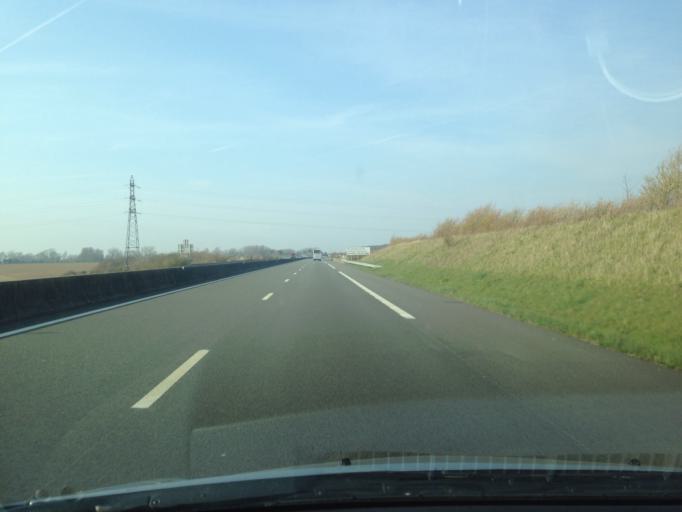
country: FR
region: Nord-Pas-de-Calais
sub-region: Departement du Pas-de-Calais
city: Verton
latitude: 50.3903
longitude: 1.6955
